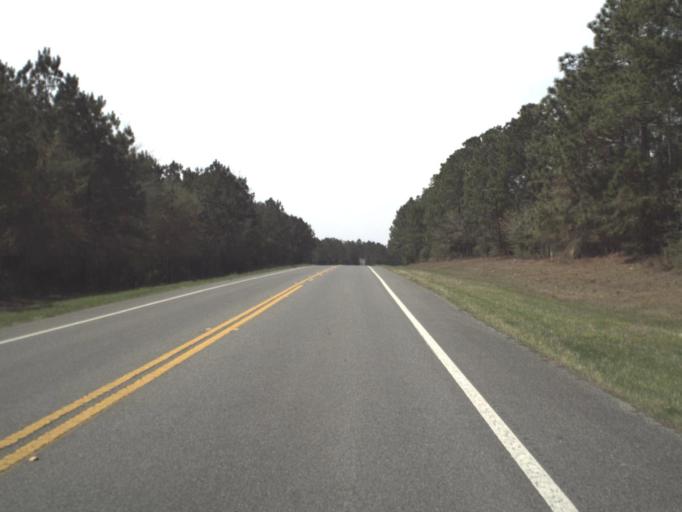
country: US
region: Florida
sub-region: Walton County
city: DeFuniak Springs
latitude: 30.7177
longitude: -86.0077
